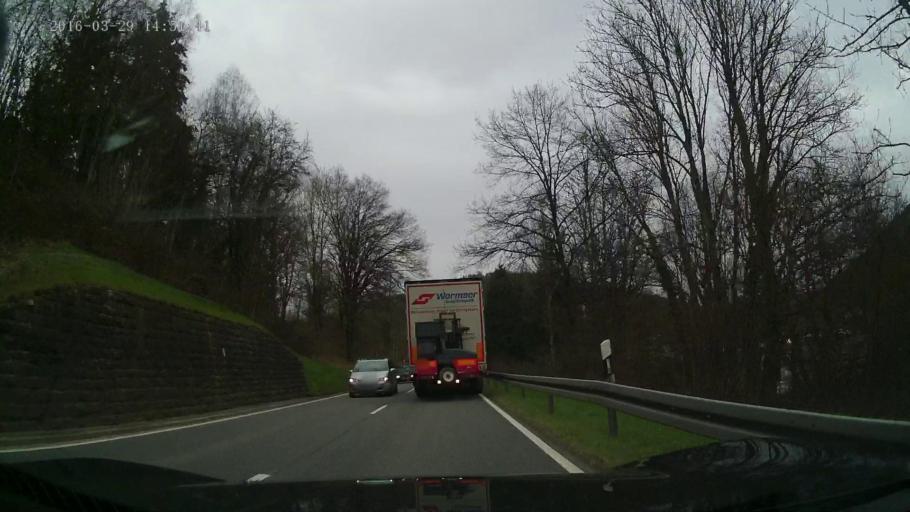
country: DE
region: Bavaria
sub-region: Regierungsbezirk Unterfranken
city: Miltenberg
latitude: 49.6263
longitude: 9.2877
